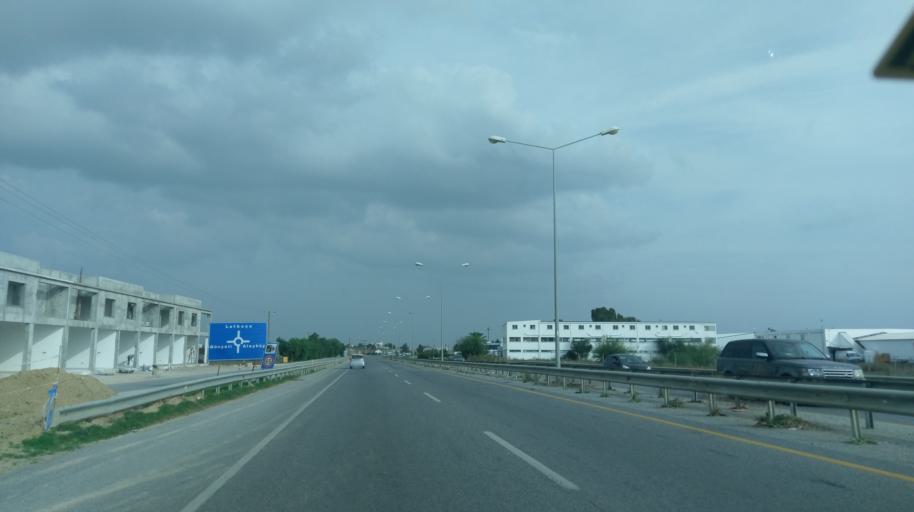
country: CY
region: Lefkosia
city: Mammari
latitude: 35.2132
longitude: 33.2738
